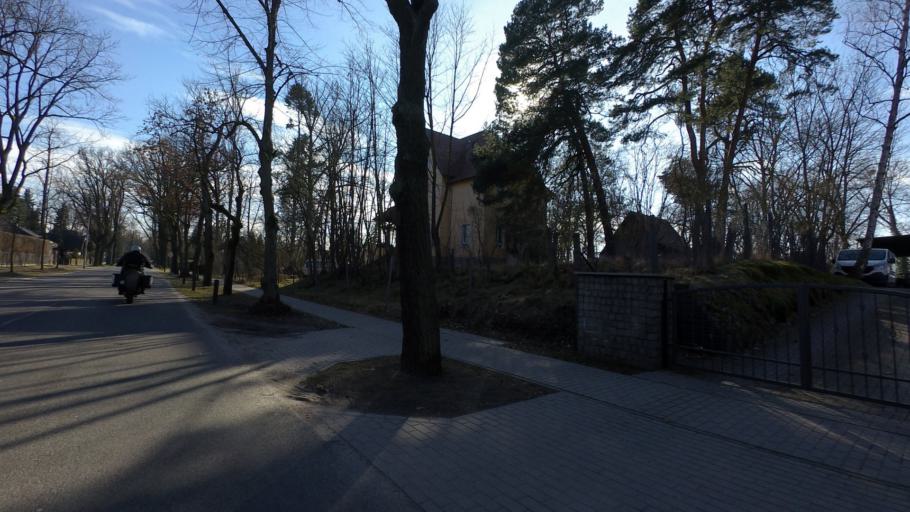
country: DE
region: Brandenburg
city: Oranienburg
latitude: 52.7507
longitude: 13.2677
